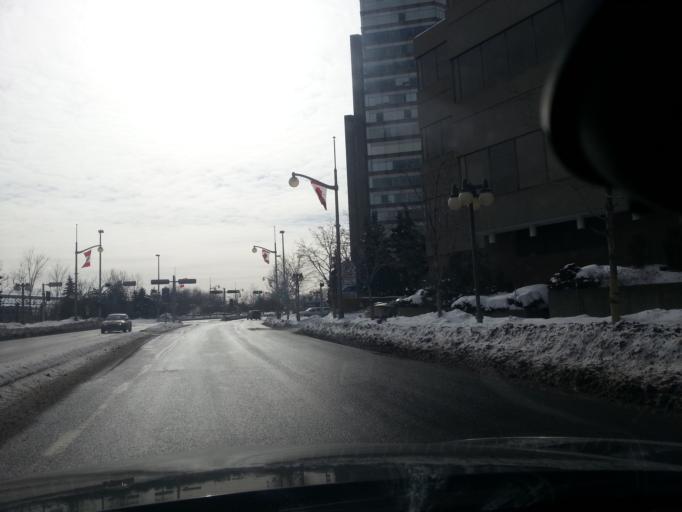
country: CA
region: Ontario
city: Ottawa
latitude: 45.4267
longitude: -75.7110
